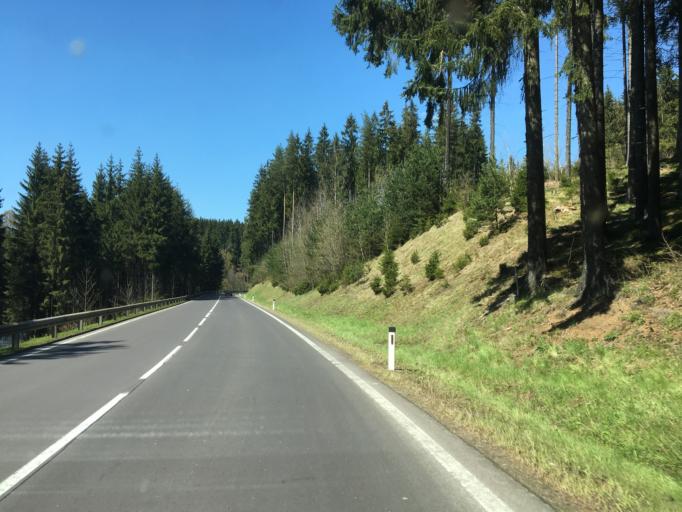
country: AT
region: Upper Austria
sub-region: Politischer Bezirk Urfahr-Umgebung
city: Bad Leonfelden
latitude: 48.4908
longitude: 14.2978
